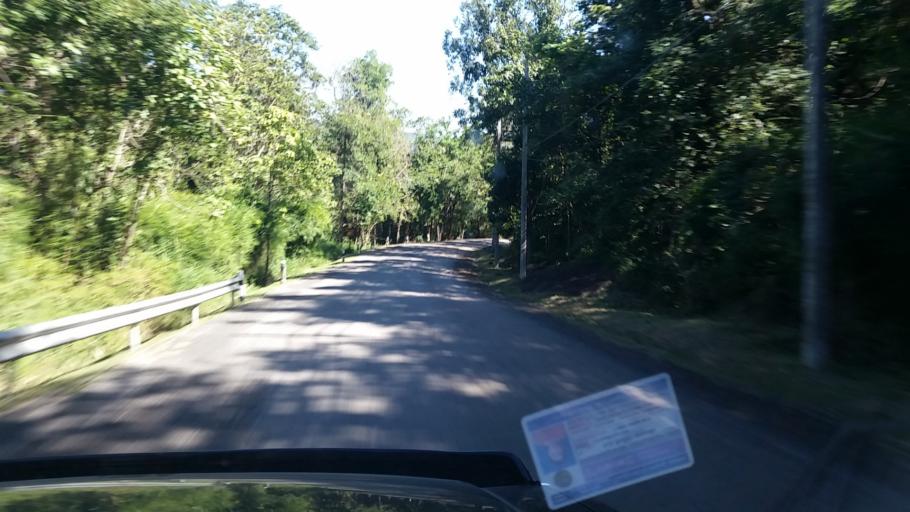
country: TH
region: Chaiyaphum
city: Chaiyaphum
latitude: 15.9806
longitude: 102.0274
